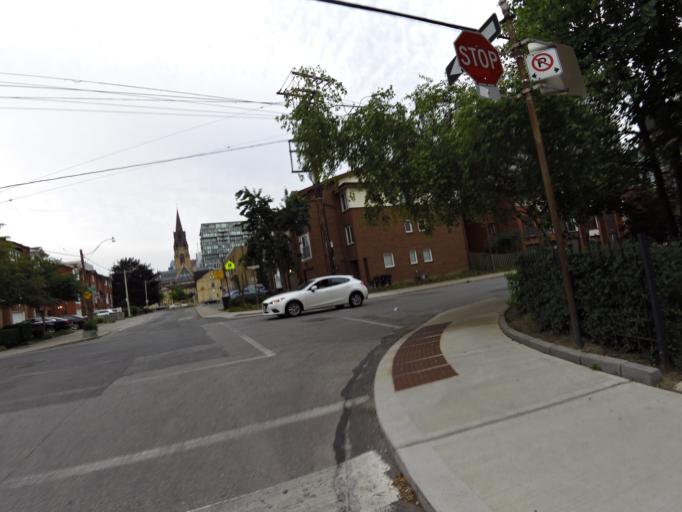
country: CA
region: Ontario
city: Toronto
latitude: 43.6446
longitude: -79.4060
